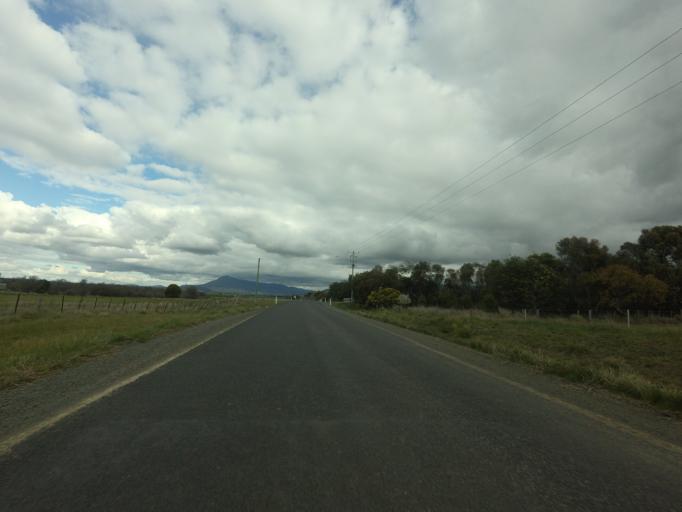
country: AU
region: Tasmania
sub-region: Northern Midlands
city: Longford
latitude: -41.7811
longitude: 147.0968
